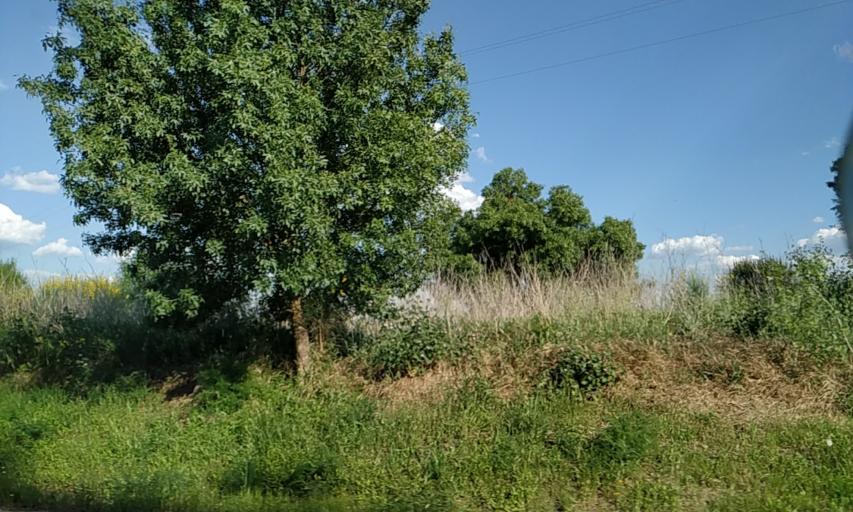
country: PT
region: Evora
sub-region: Estremoz
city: Estremoz
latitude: 38.9669
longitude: -7.4952
